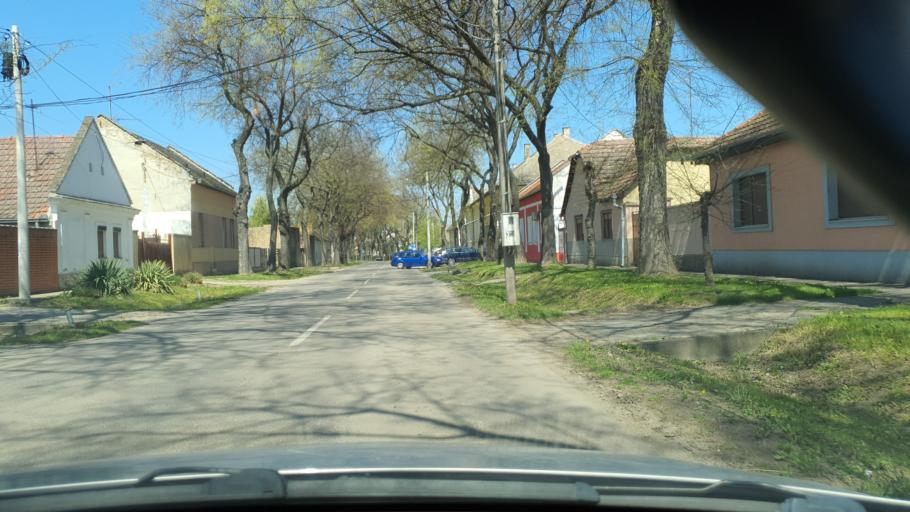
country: RS
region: Autonomna Pokrajina Vojvodina
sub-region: Zapadnobacki Okrug
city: Sombor
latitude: 45.7644
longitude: 19.1094
